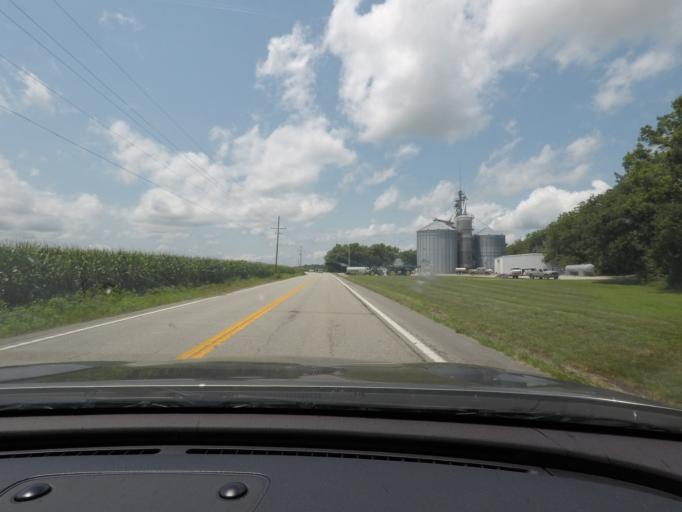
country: US
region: Missouri
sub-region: Carroll County
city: Carrollton
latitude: 39.1952
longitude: -93.4178
